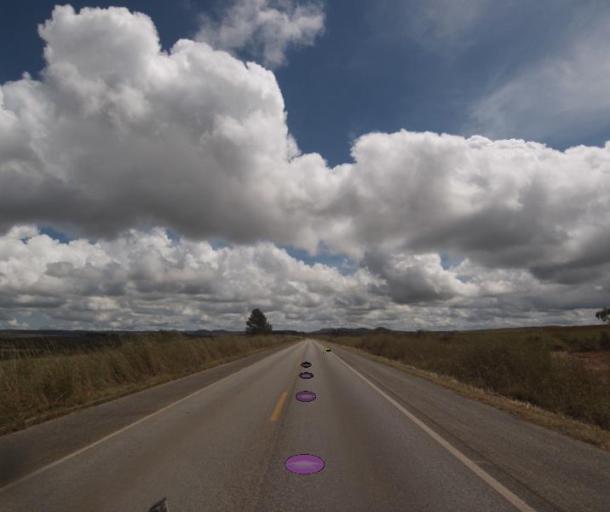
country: BR
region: Goias
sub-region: Pirenopolis
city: Pirenopolis
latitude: -15.7493
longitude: -48.6574
